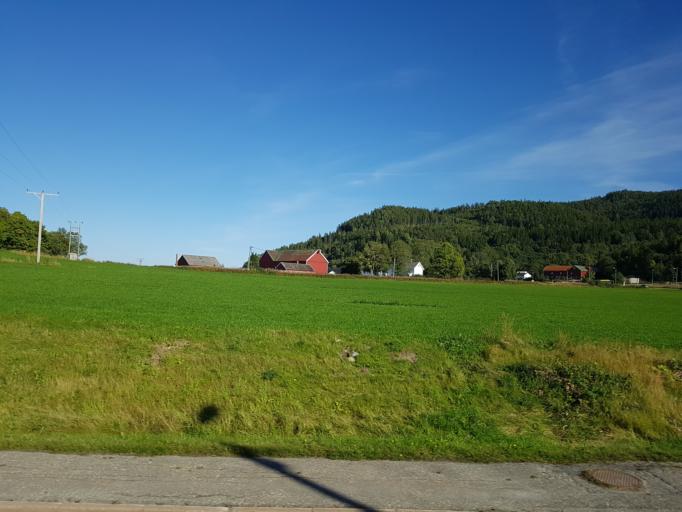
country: NO
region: Sor-Trondelag
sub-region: Skaun
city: Borsa
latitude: 63.4465
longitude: 10.1922
